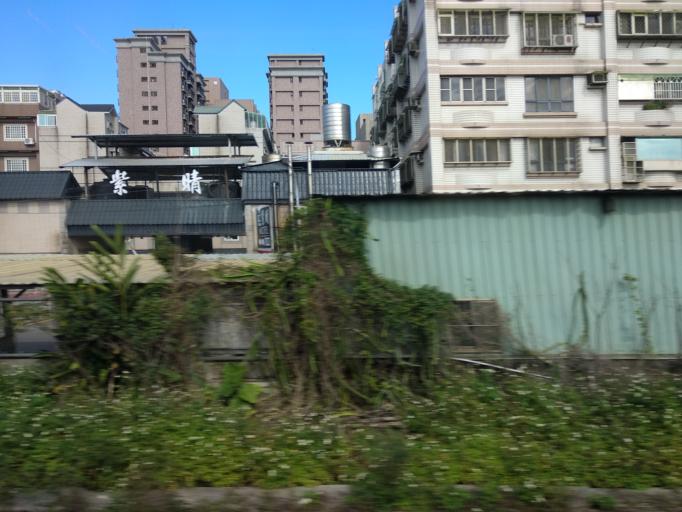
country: TW
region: Taiwan
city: Taoyuan City
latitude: 24.9843
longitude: 121.2925
